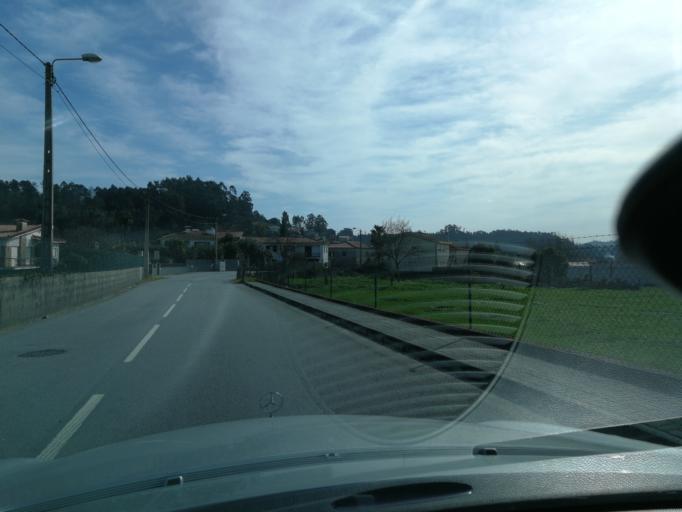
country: PT
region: Braga
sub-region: Vila Nova de Famalicao
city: Vila Nova de Famalicao
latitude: 41.4366
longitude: -8.5218
